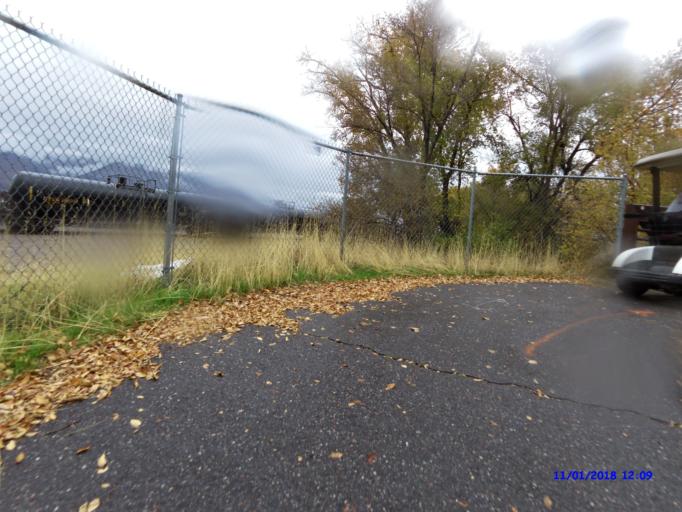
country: US
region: Utah
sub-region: Weber County
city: Ogden
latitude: 41.2273
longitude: -111.9869
